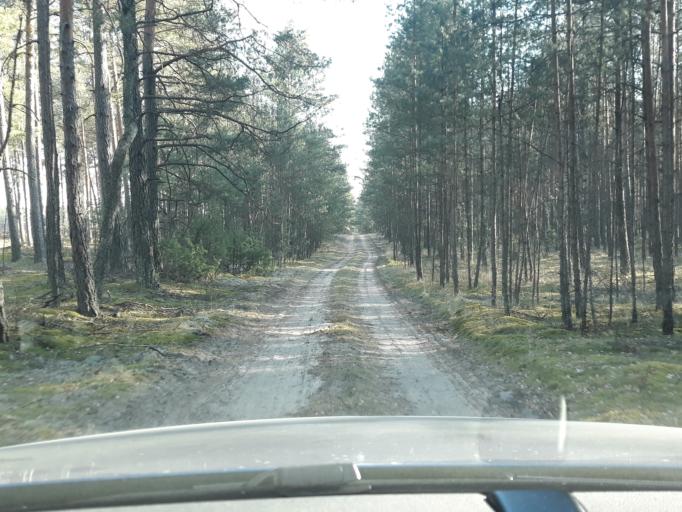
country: PL
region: Pomeranian Voivodeship
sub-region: Powiat bytowski
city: Lipnica
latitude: 53.9110
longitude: 17.4970
